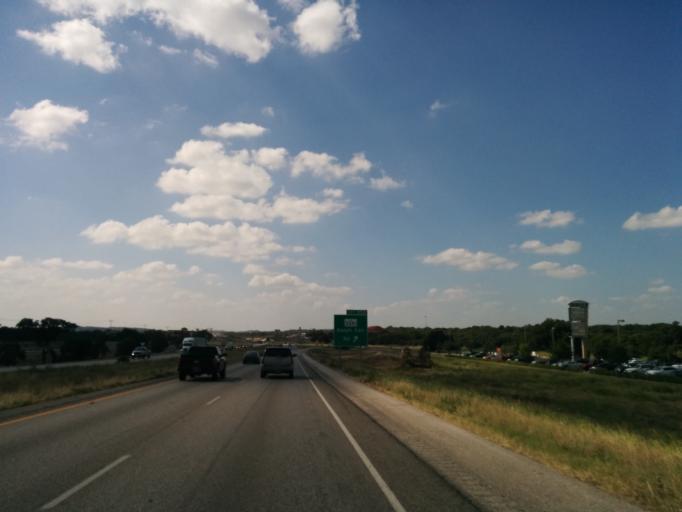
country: US
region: Texas
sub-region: Bexar County
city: Cross Mountain
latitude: 29.6679
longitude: -98.6320
